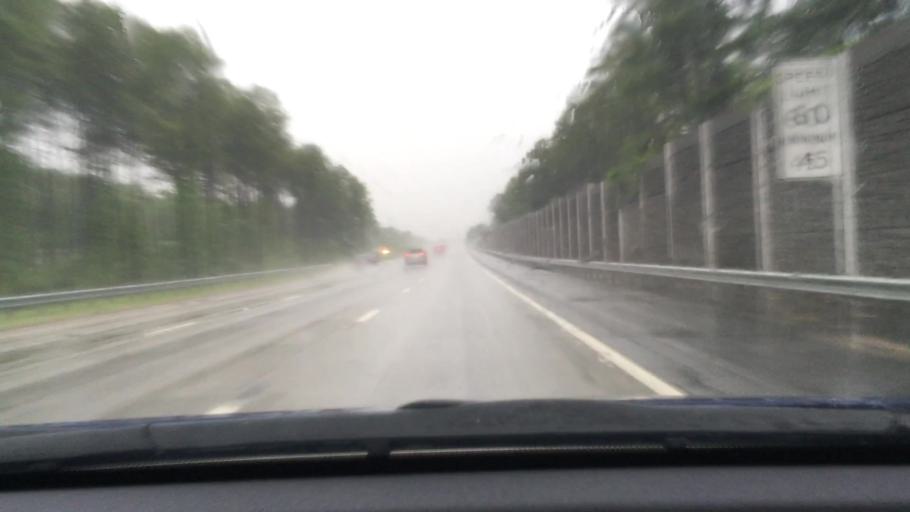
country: US
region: South Carolina
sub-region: Richland County
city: Woodfield
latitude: 34.0896
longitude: -80.8694
